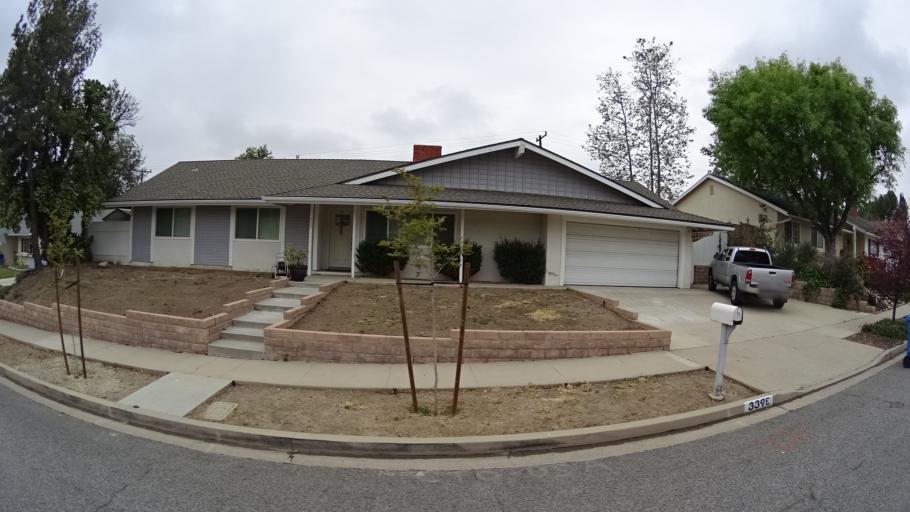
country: US
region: California
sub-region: Ventura County
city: Thousand Oaks
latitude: 34.2056
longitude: -118.8703
